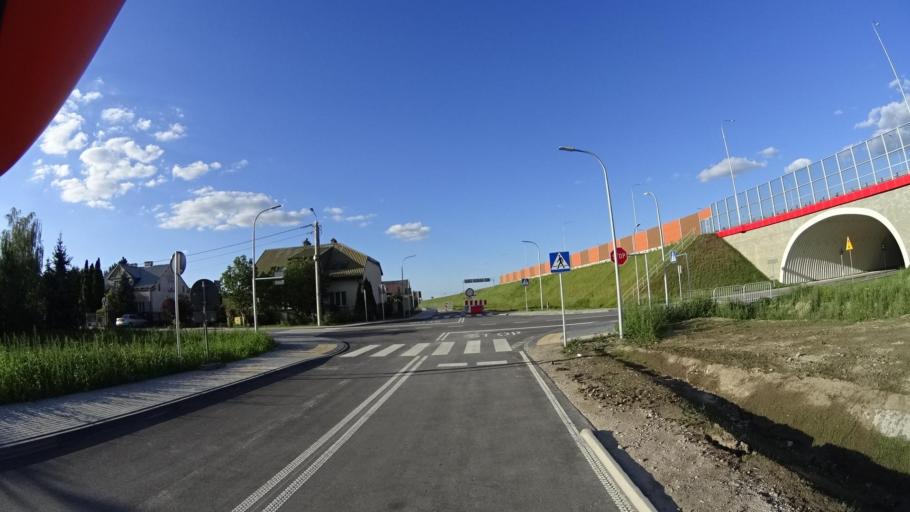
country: PL
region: Masovian Voivodeship
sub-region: Powiat piaseczynski
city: Lesznowola
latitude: 52.0928
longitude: 20.9699
